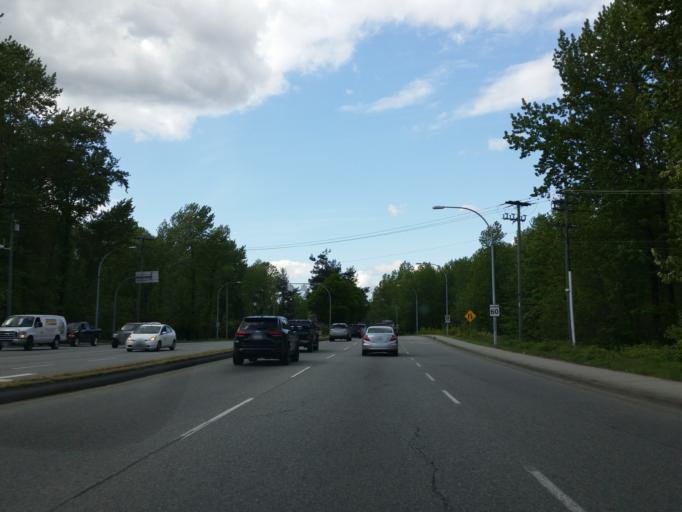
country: CA
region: British Columbia
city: Coquitlam
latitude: 49.2679
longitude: -122.7771
